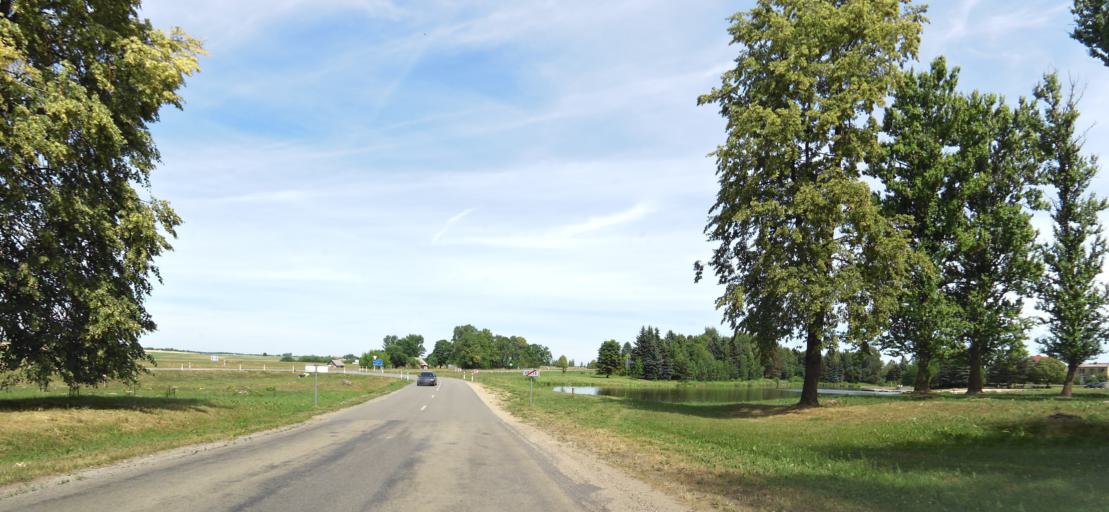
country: LT
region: Panevezys
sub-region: Panevezys City
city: Panevezys
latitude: 55.6535
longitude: 24.2317
